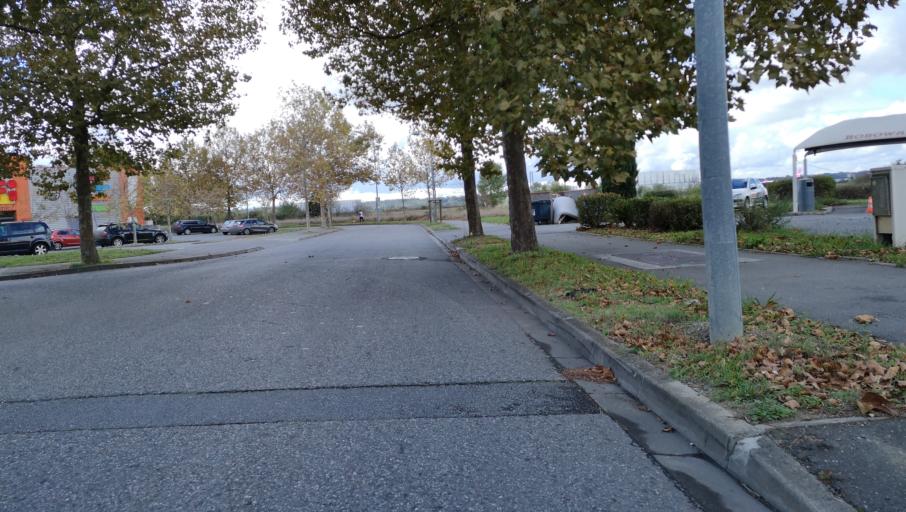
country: FR
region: Midi-Pyrenees
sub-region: Departement de la Haute-Garonne
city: Beauzelle
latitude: 43.6446
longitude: 1.3661
